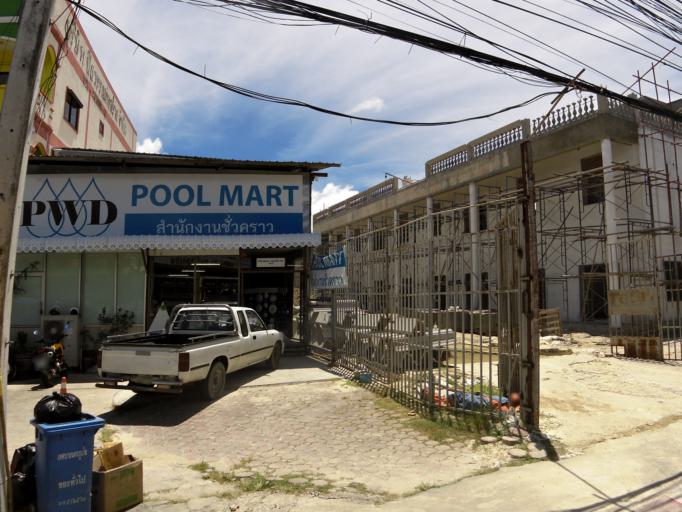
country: TH
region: Phuket
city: Ban Talat Nua
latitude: 7.8845
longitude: 98.3800
